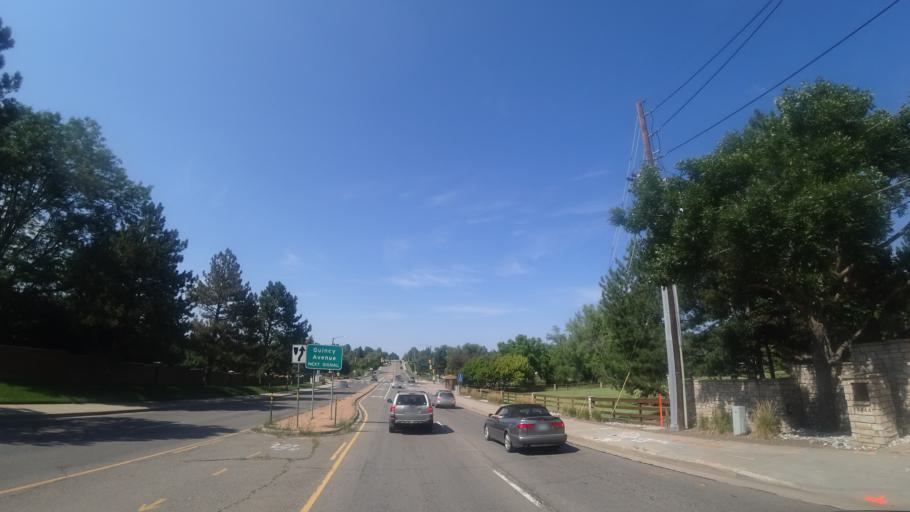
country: US
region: Colorado
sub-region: Arapahoe County
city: Cherry Hills Village
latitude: 39.6364
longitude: -104.9596
